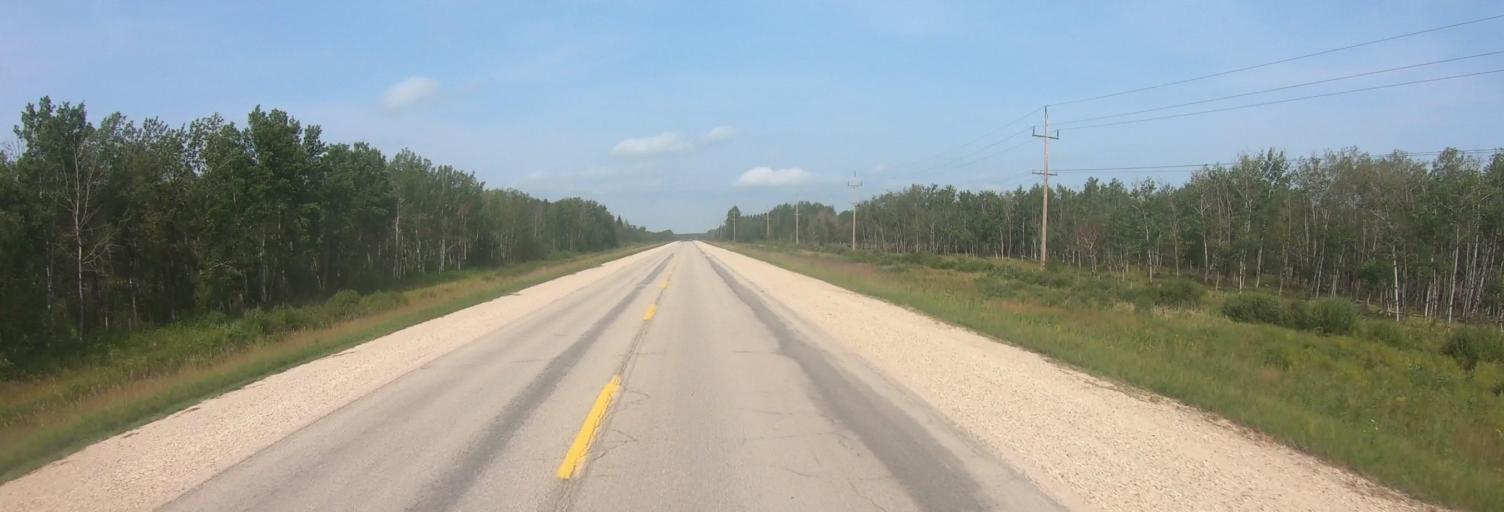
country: CA
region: Manitoba
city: Steinbach
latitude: 49.3626
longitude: -96.6740
